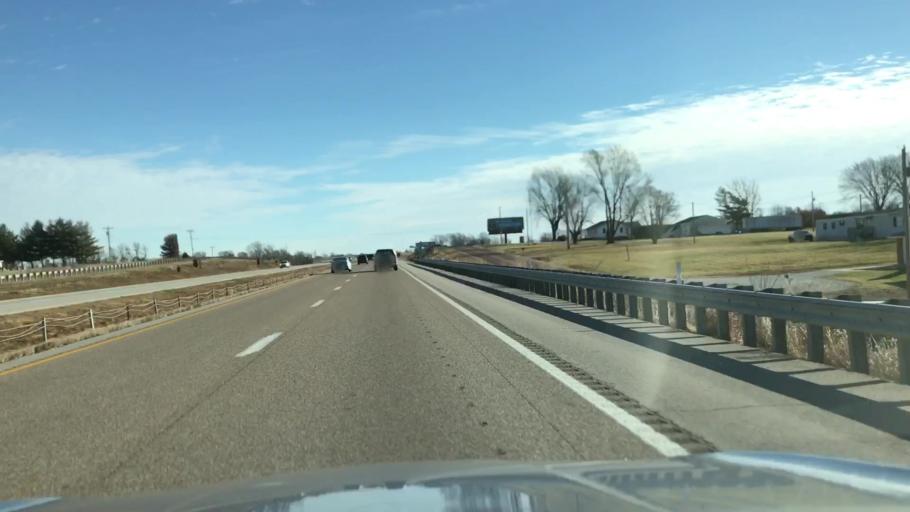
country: US
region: Missouri
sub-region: Cooper County
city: Boonville
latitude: 38.9348
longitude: -92.8713
